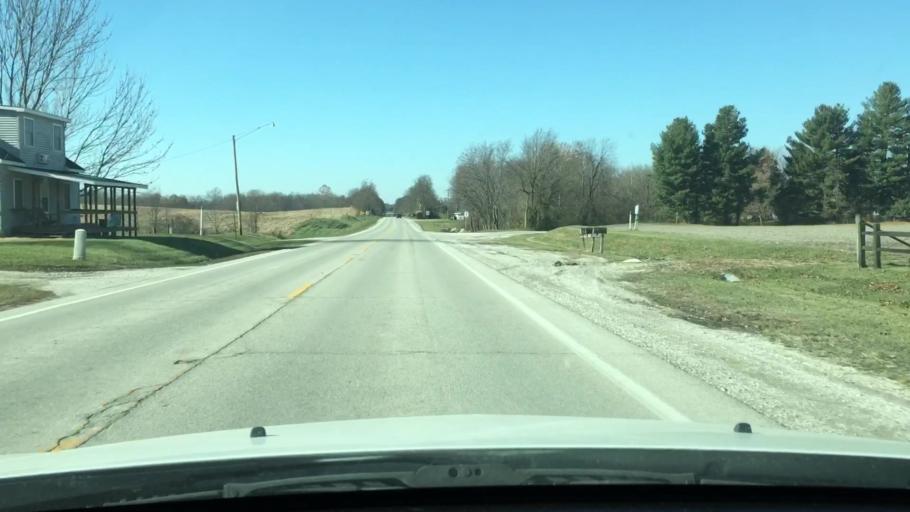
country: US
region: Illinois
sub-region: Pike County
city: Griggsville
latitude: 39.6201
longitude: -90.6809
